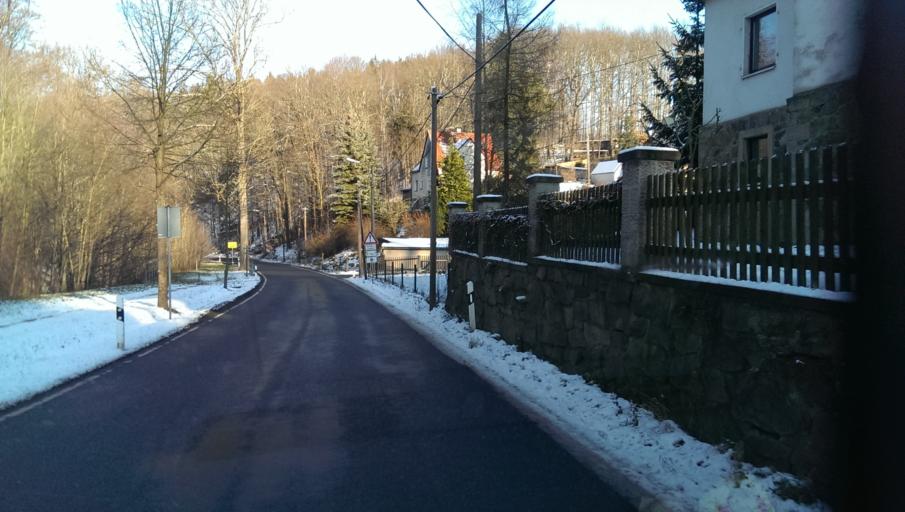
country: DE
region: Saxony
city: Dorfhain
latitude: 50.9376
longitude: 13.5873
